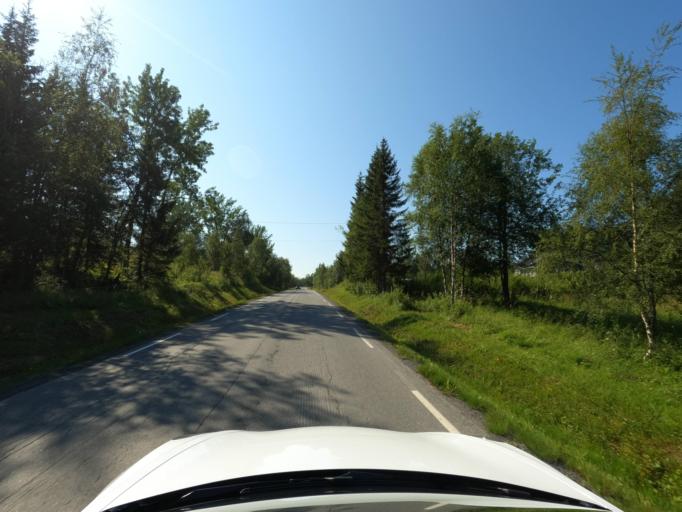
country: NO
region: Nordland
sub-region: Ballangen
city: Ballangen
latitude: 68.3595
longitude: 16.8762
